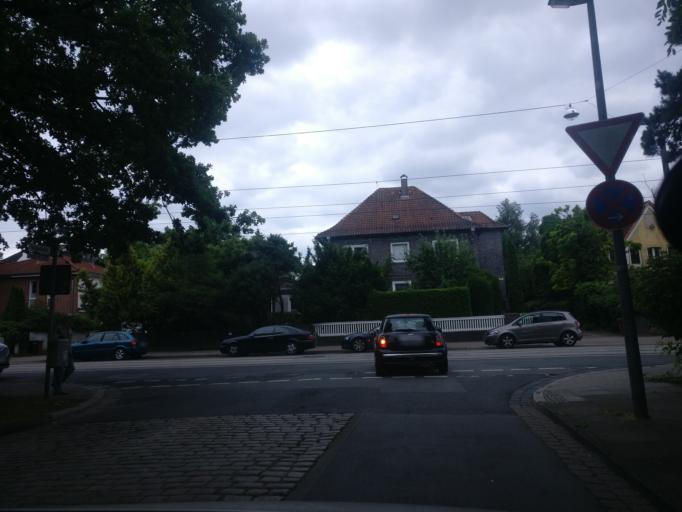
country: DE
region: Lower Saxony
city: Laatzen
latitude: 52.3615
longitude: 9.8325
